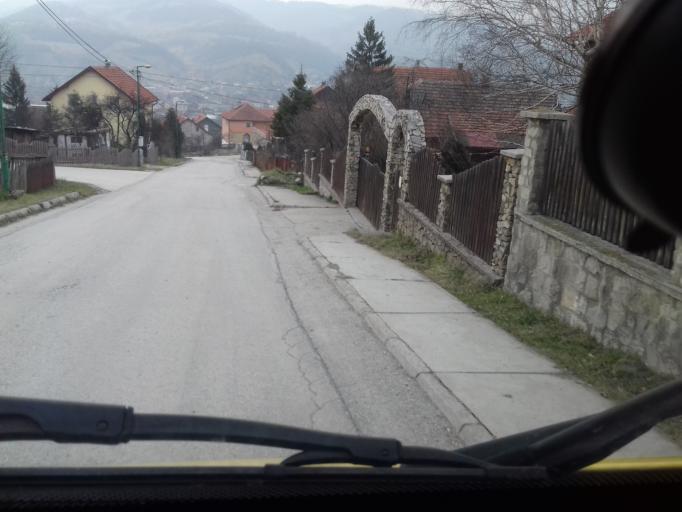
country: BA
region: Federation of Bosnia and Herzegovina
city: Kakanj
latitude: 44.1285
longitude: 18.1100
